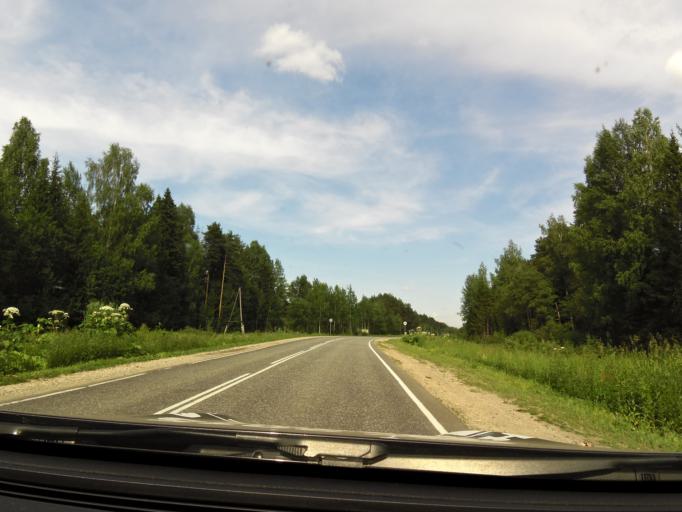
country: RU
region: Kirov
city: Slobodskoy
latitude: 58.7741
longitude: 50.3805
